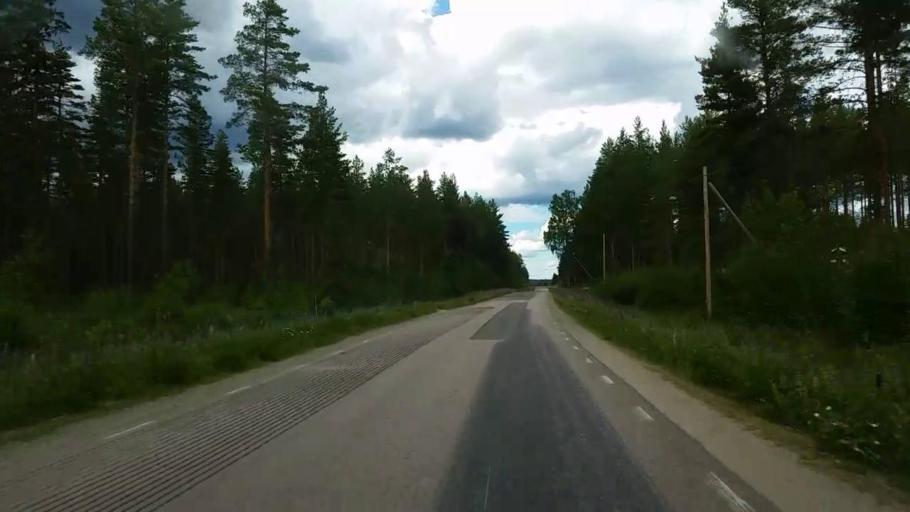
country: SE
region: Gaevleborg
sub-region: Ovanakers Kommun
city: Edsbyn
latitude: 61.4092
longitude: 15.8970
